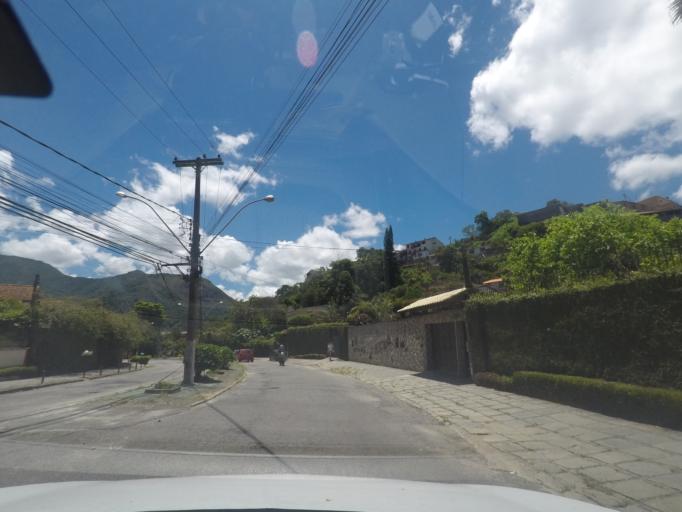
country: BR
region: Rio de Janeiro
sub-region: Teresopolis
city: Teresopolis
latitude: -22.4340
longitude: -42.9689
